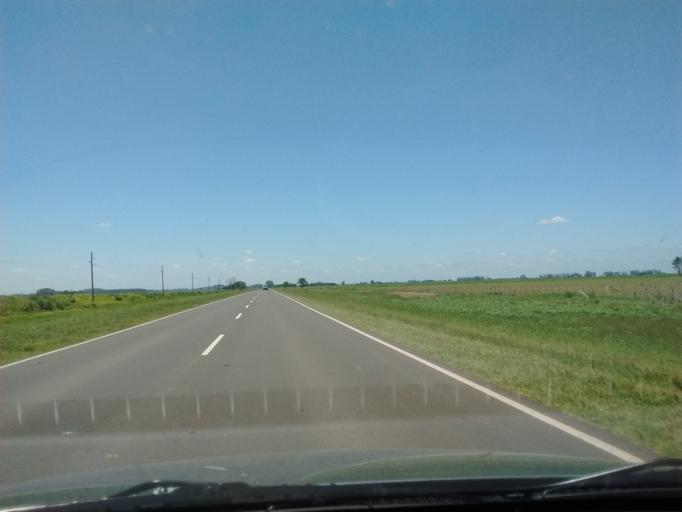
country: AR
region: Entre Rios
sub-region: Departamento de Gualeguay
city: Gualeguay
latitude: -33.0705
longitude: -59.4054
